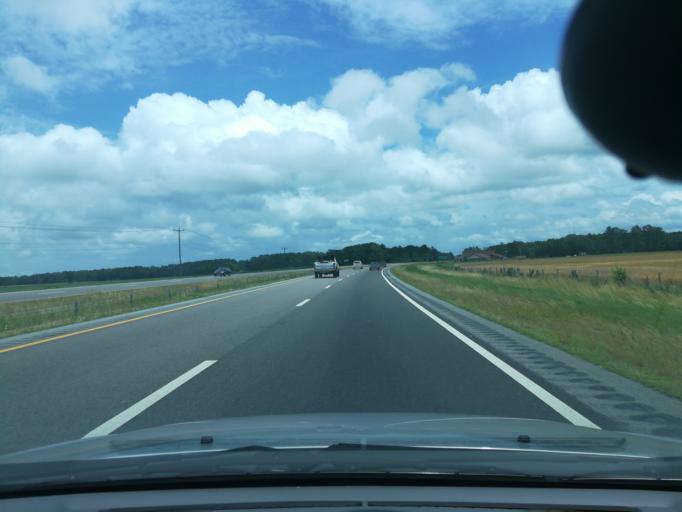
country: US
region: North Carolina
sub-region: Tyrrell County
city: Columbia
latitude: 35.8997
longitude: -76.3367
